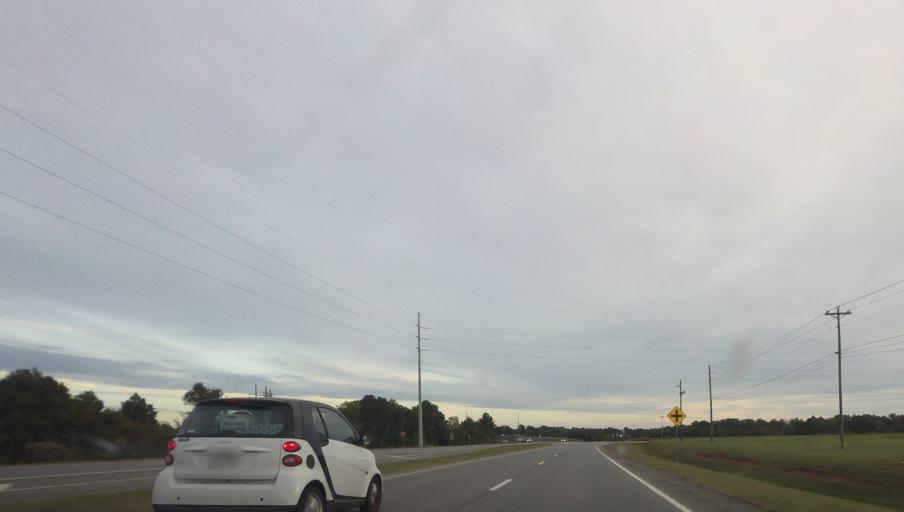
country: US
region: Georgia
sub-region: Houston County
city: Perry
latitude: 32.4675
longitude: -83.6982
